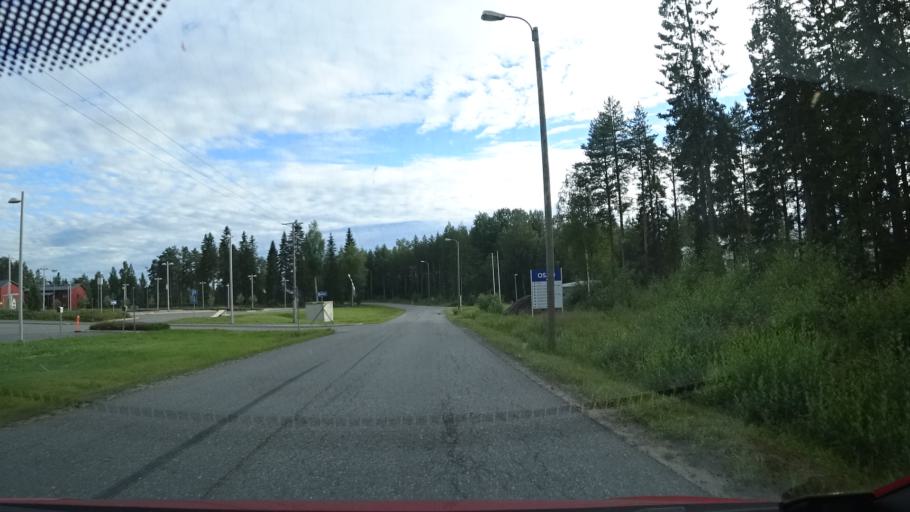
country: FI
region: Northern Ostrobothnia
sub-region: Oulu
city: Haukipudas
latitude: 65.1966
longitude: 25.4126
